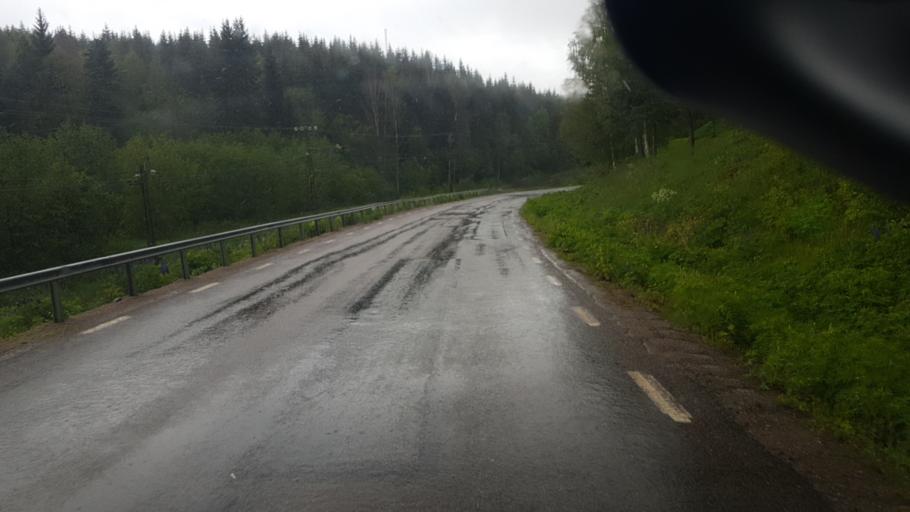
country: SE
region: Vaermland
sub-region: Eda Kommun
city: Amotfors
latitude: 59.6987
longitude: 12.4596
